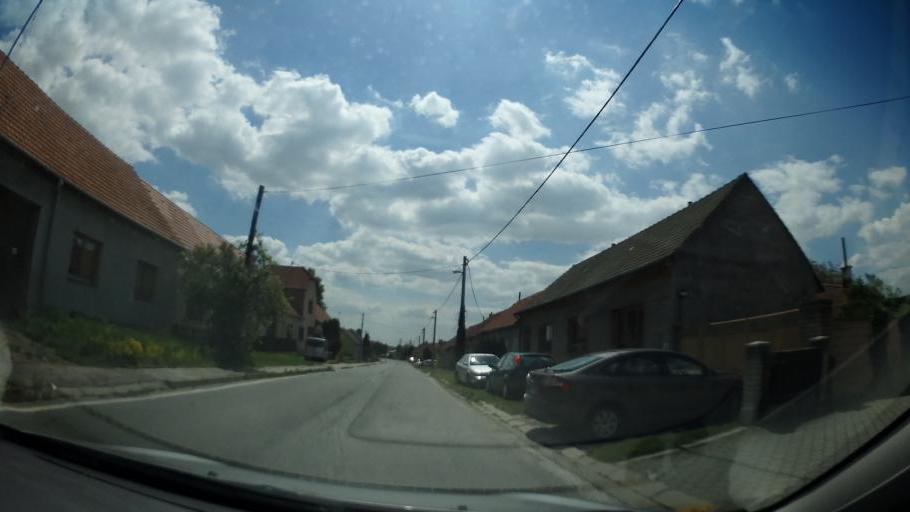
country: CZ
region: Vysocina
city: Hrotovice
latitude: 49.1353
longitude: 16.0805
